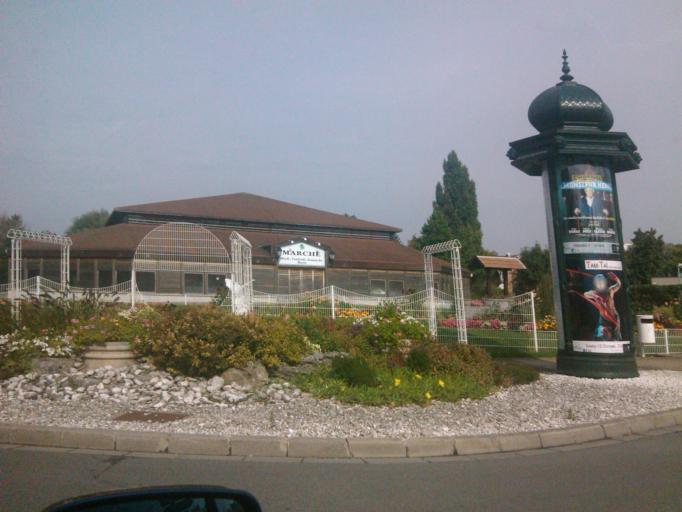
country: FR
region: Ile-de-France
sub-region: Departement des Yvelines
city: Plaisir
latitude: 48.8175
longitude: 1.9446
